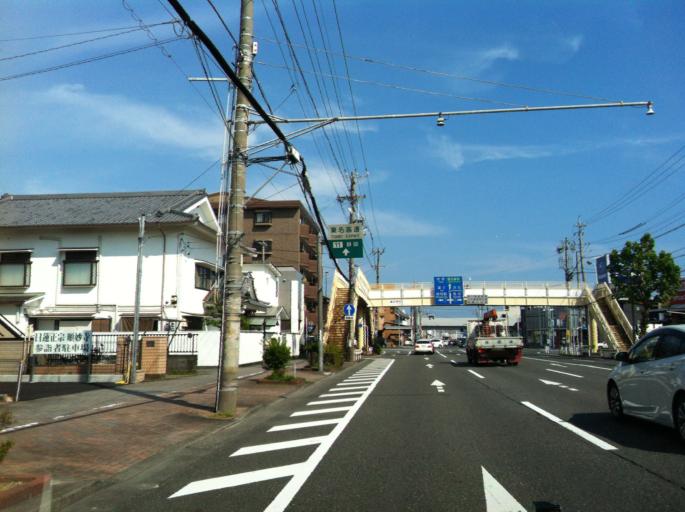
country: JP
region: Shizuoka
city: Shizuoka-shi
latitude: 34.9622
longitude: 138.3738
